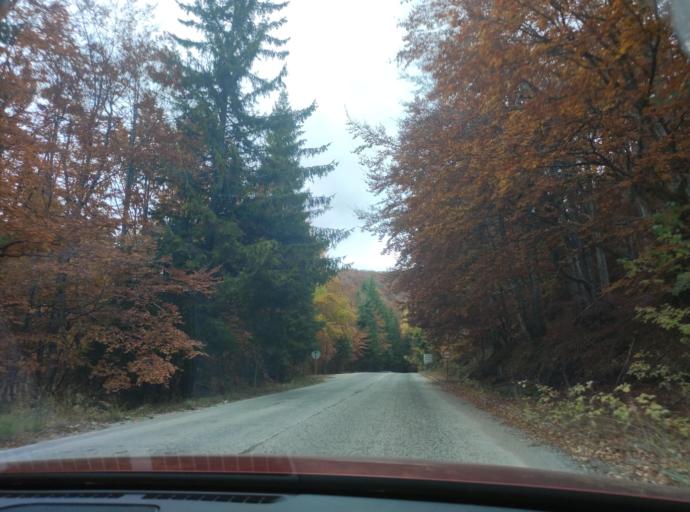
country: BG
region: Sofiya
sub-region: Obshtina Godech
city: Godech
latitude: 43.1123
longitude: 23.1123
